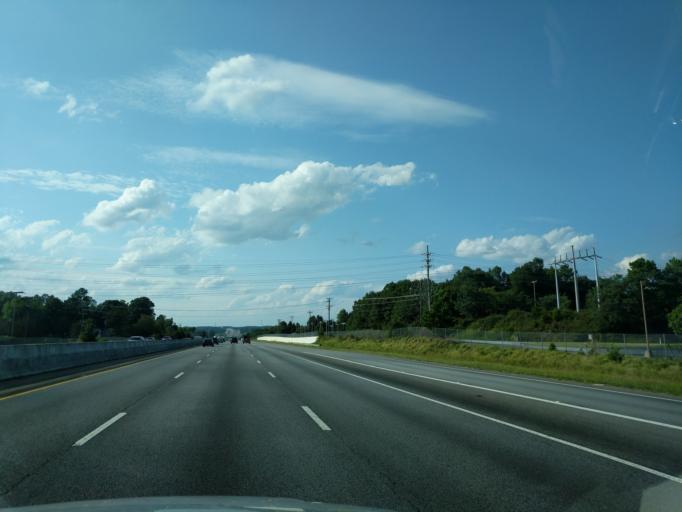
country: US
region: South Carolina
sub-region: Greenville County
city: Simpsonville
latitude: 34.7225
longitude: -82.2581
